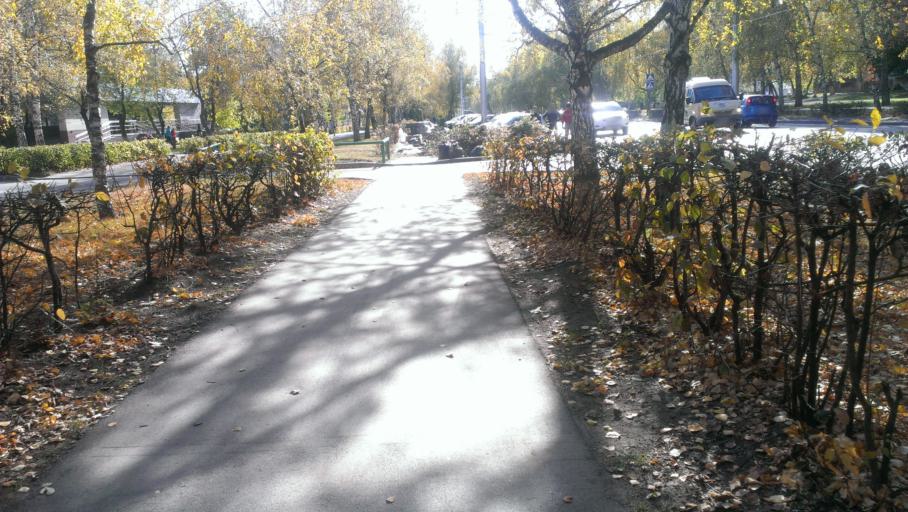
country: RU
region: Altai Krai
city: Novosilikatnyy
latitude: 53.3534
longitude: 83.6843
